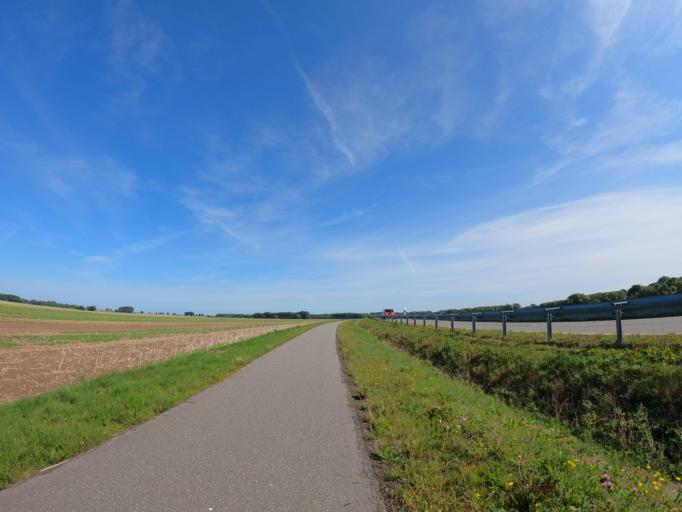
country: DE
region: Mecklenburg-Vorpommern
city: Kramerhof
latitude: 54.3550
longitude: 13.0496
